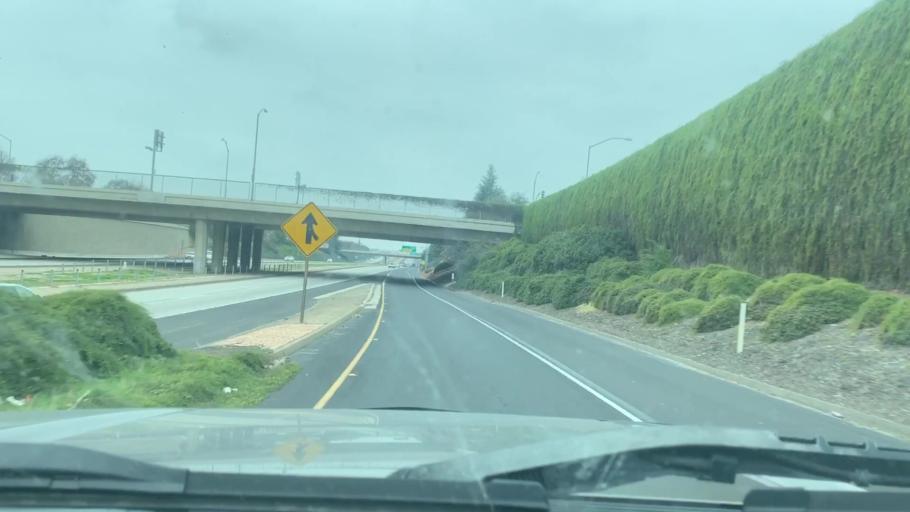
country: US
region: California
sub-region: Tulare County
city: Visalia
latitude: 36.3277
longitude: -119.3352
